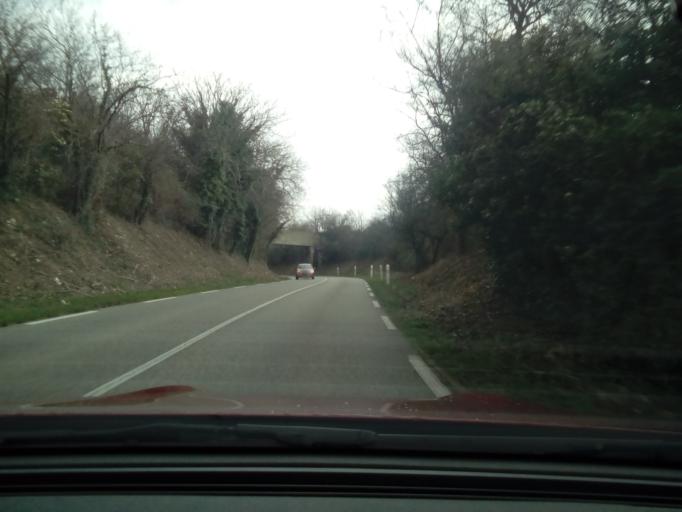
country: FR
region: Rhone-Alpes
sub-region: Departement de l'Ardeche
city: Cruas
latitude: 44.6656
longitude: 4.7668
